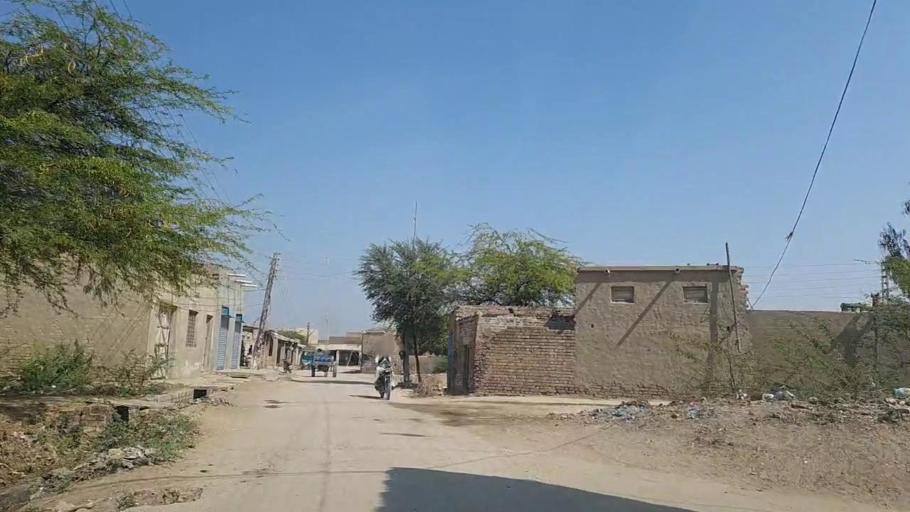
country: PK
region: Sindh
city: Naukot
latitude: 24.8620
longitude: 69.4056
